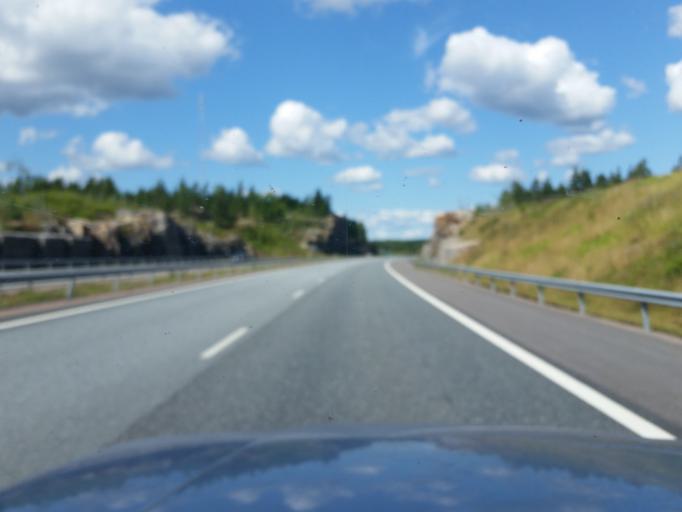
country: FI
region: Uusimaa
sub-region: Helsinki
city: Sammatti
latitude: 60.3720
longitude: 23.8366
